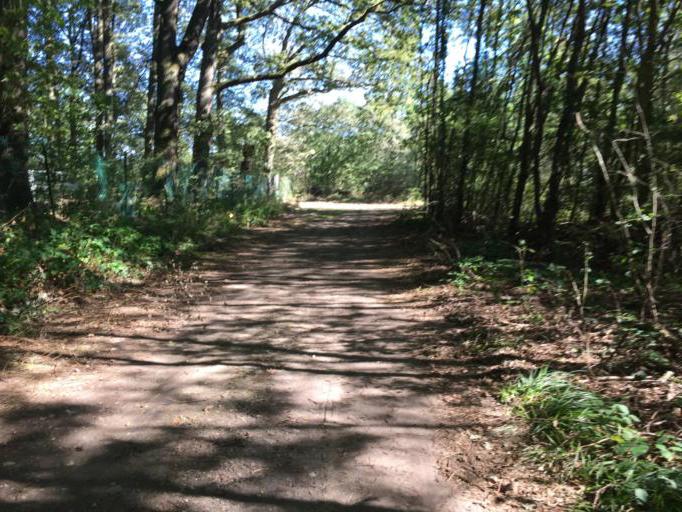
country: FR
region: Ile-de-France
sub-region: Departement de l'Essonne
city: Orsay
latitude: 48.6905
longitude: 2.1903
